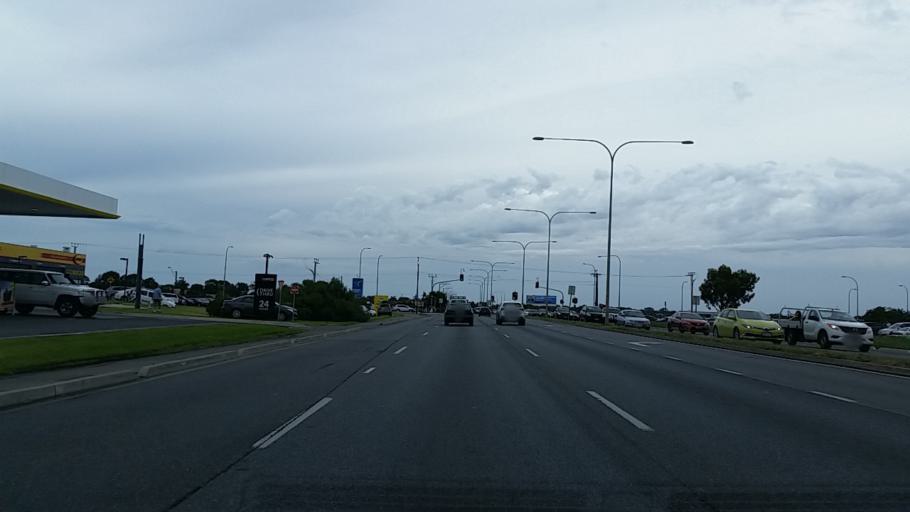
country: AU
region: South Australia
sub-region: City of West Torrens
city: Plympton
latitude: -34.9461
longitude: 138.5177
